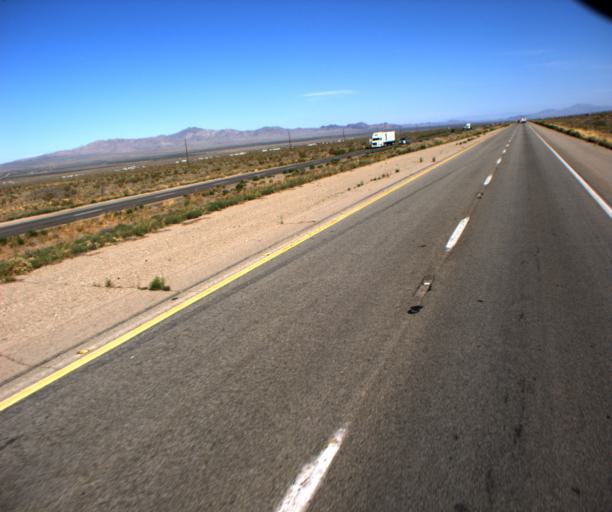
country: US
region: Arizona
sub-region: Mohave County
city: Dolan Springs
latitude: 35.4776
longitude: -114.3162
